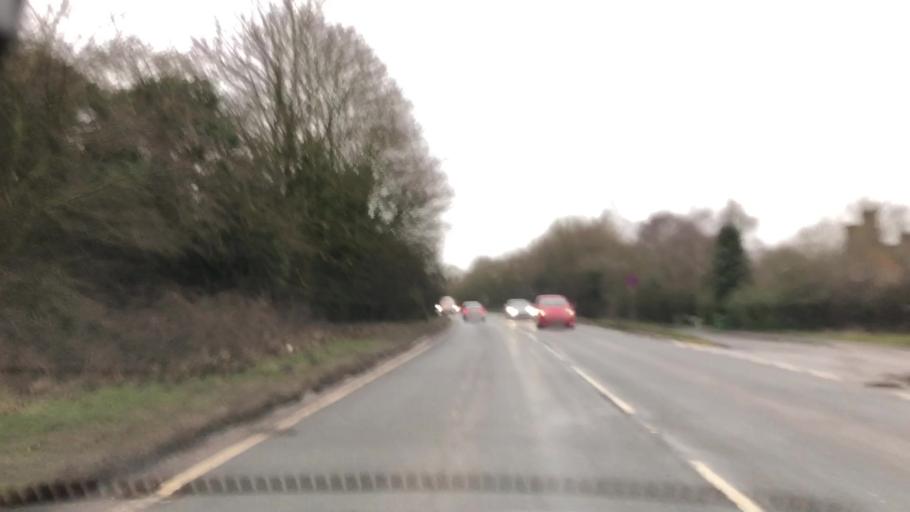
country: GB
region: England
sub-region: Warwickshire
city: Curdworth
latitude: 52.5466
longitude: -1.7101
